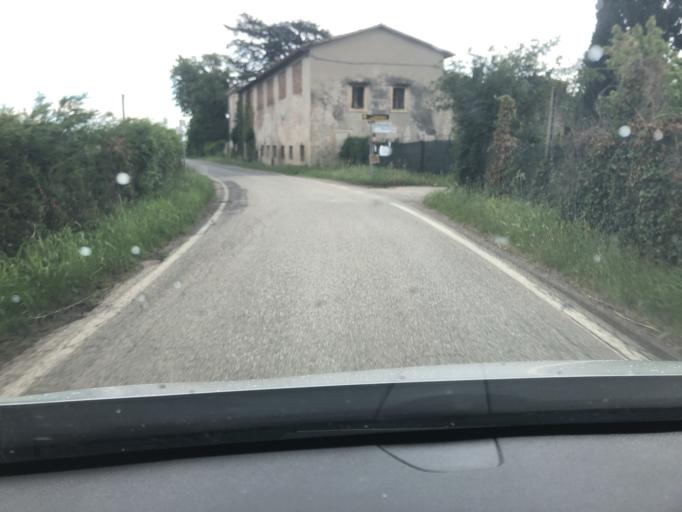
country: IT
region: Veneto
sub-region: Provincia di Verona
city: Sona
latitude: 45.4284
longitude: 10.8525
